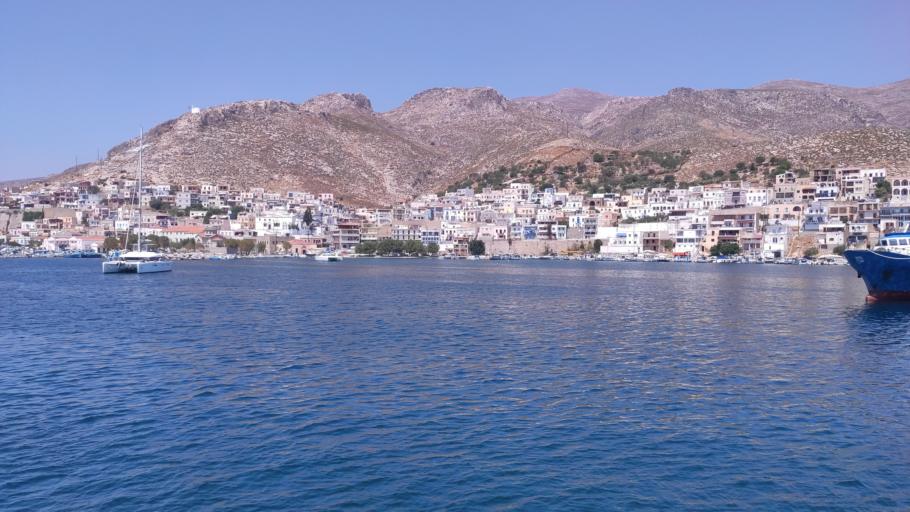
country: GR
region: South Aegean
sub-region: Nomos Dodekanisou
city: Kalymnos
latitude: 36.9487
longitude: 26.9919
